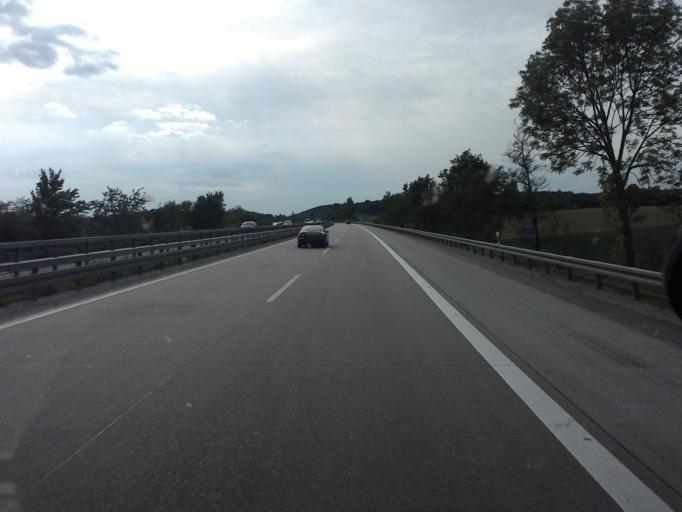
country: DE
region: Bavaria
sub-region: Lower Bavaria
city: Bogen
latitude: 48.9364
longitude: 12.6685
